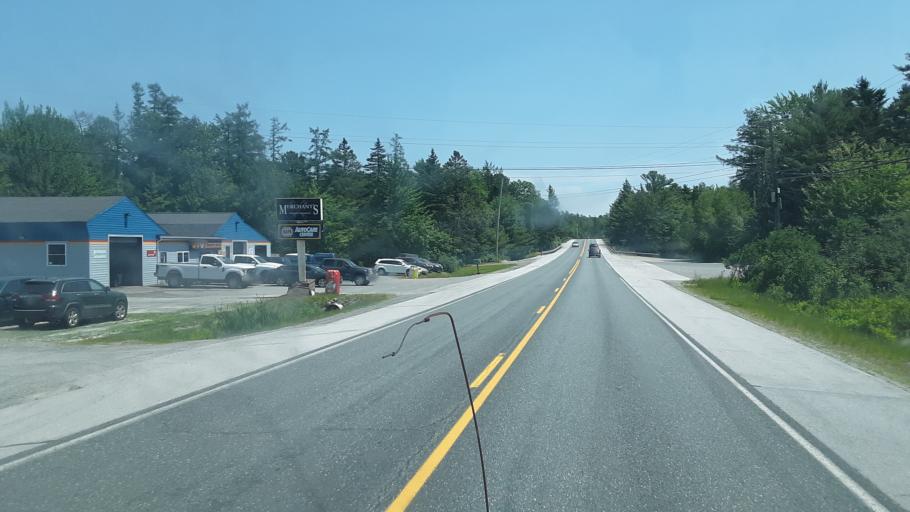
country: US
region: Maine
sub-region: Hancock County
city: Hancock
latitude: 44.5338
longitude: -68.2704
